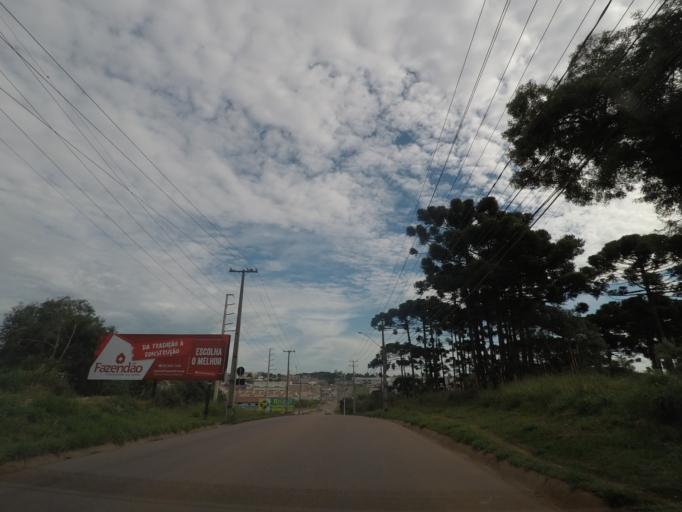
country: BR
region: Parana
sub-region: Araucaria
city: Araucaria
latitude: -25.6375
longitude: -49.2993
